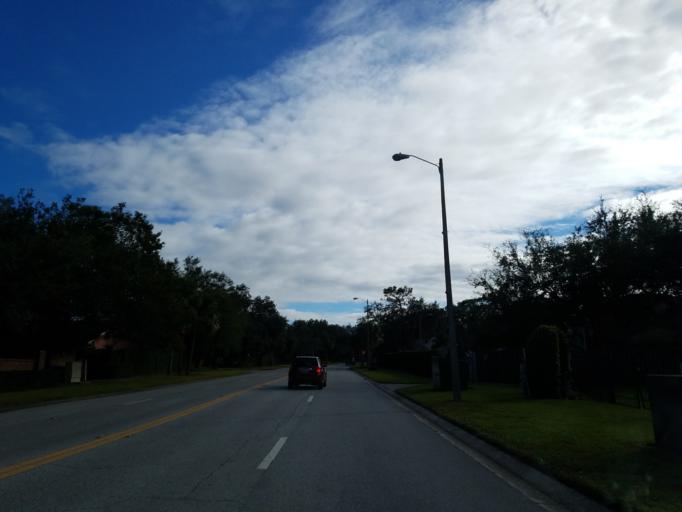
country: US
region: Florida
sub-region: Hillsborough County
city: Bloomingdale
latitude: 27.8852
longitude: -82.2402
